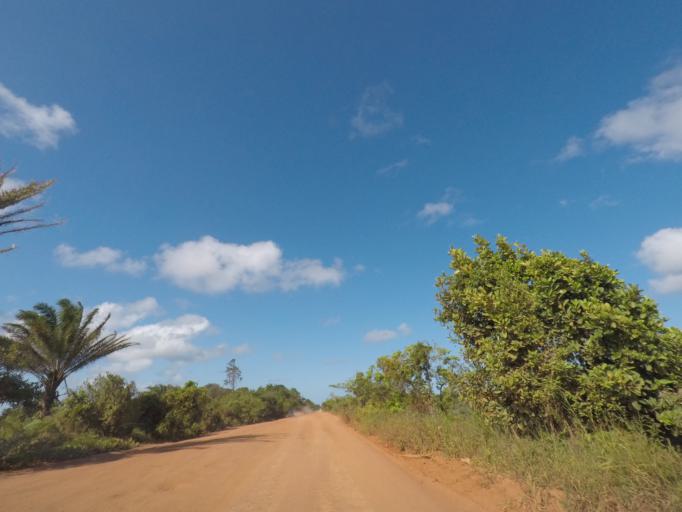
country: BR
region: Bahia
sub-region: Marau
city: Marau
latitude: -14.1524
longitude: -39.0071
